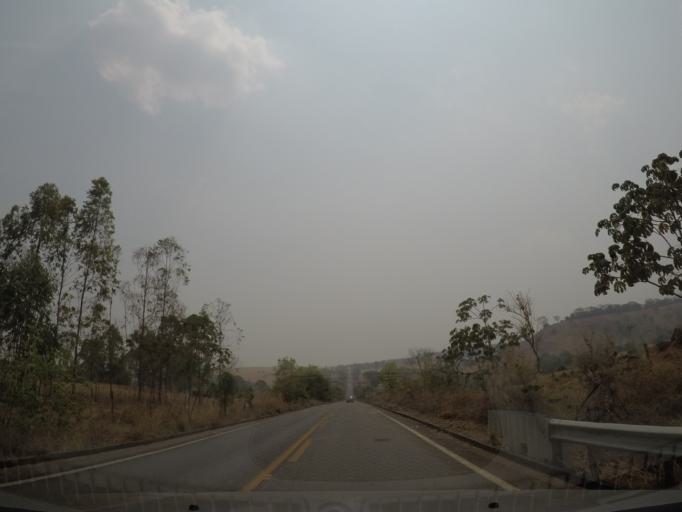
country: BR
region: Goias
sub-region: Pirenopolis
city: Pirenopolis
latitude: -15.8990
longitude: -48.8721
